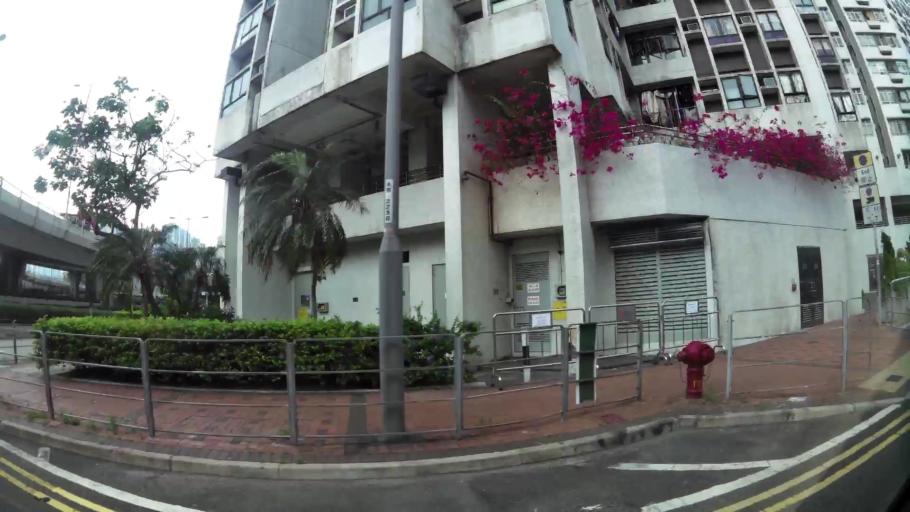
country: HK
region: Kowloon City
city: Kowloon
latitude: 22.3098
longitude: 114.1680
